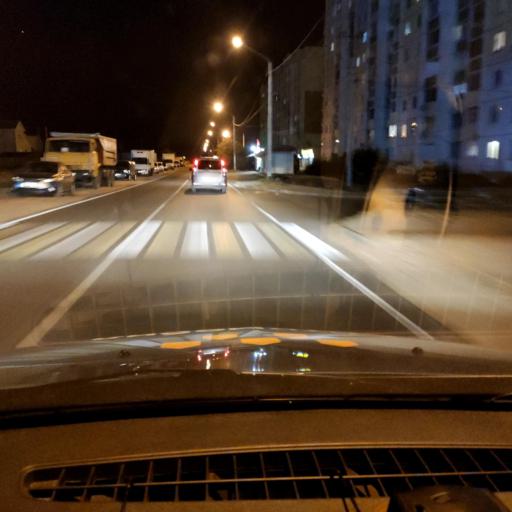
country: RU
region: Voronezj
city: Pridonskoy
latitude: 51.6208
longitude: 39.0658
